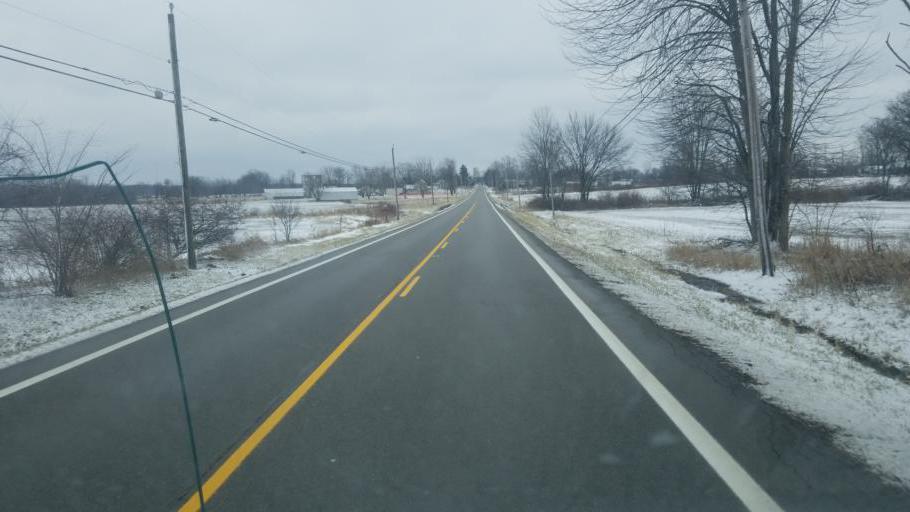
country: US
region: Ohio
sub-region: Licking County
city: Johnstown
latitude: 40.1785
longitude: -82.7359
